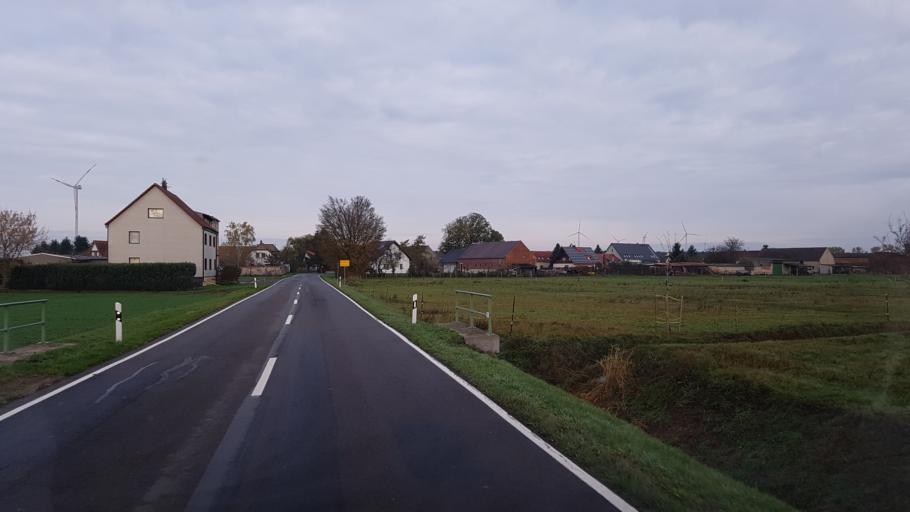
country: DE
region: Brandenburg
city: Doberlug-Kirchhain
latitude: 51.6853
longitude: 13.5115
